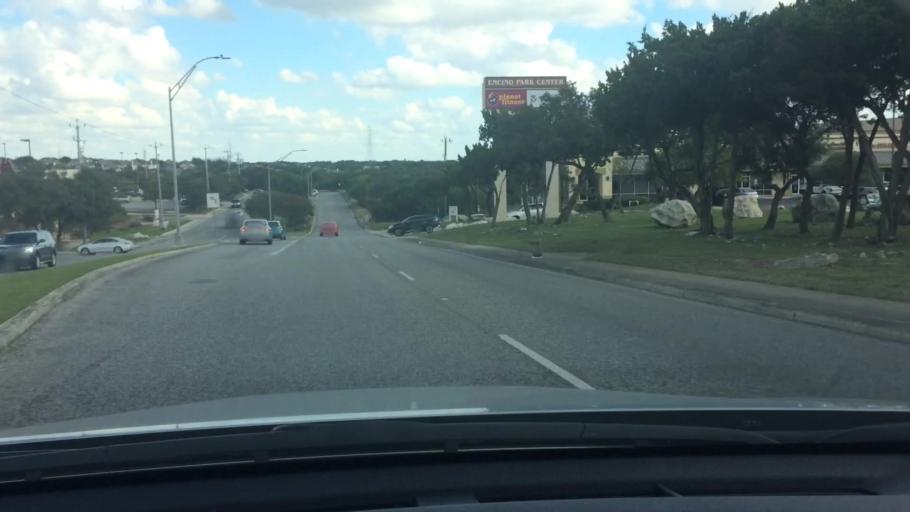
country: US
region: Texas
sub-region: Bexar County
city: Hollywood Park
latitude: 29.6363
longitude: -98.4549
